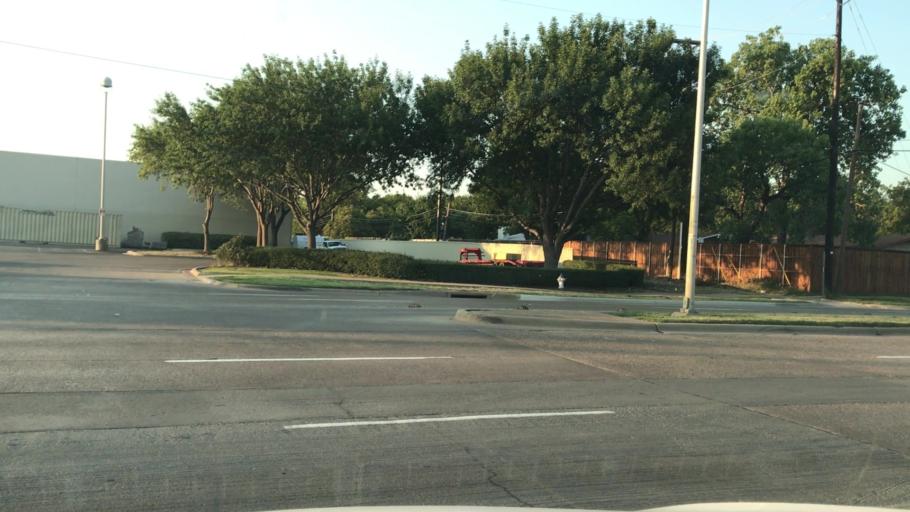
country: US
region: Texas
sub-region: Dallas County
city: Farmers Branch
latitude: 32.9094
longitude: -96.8696
